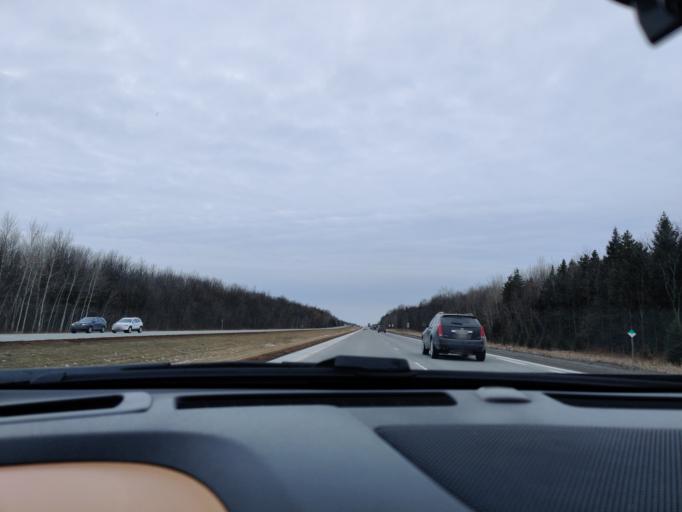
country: US
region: New York
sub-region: St. Lawrence County
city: Ogdensburg
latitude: 44.8555
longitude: -75.3339
